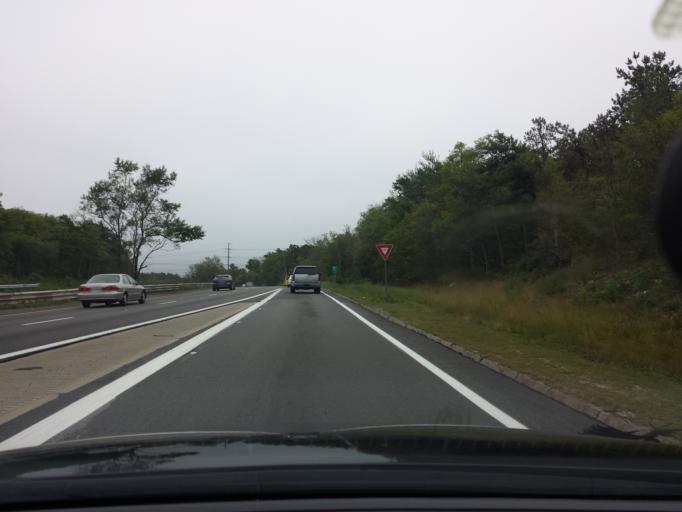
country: US
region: Massachusetts
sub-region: Barnstable County
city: Sagamore
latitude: 41.7671
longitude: -70.5433
